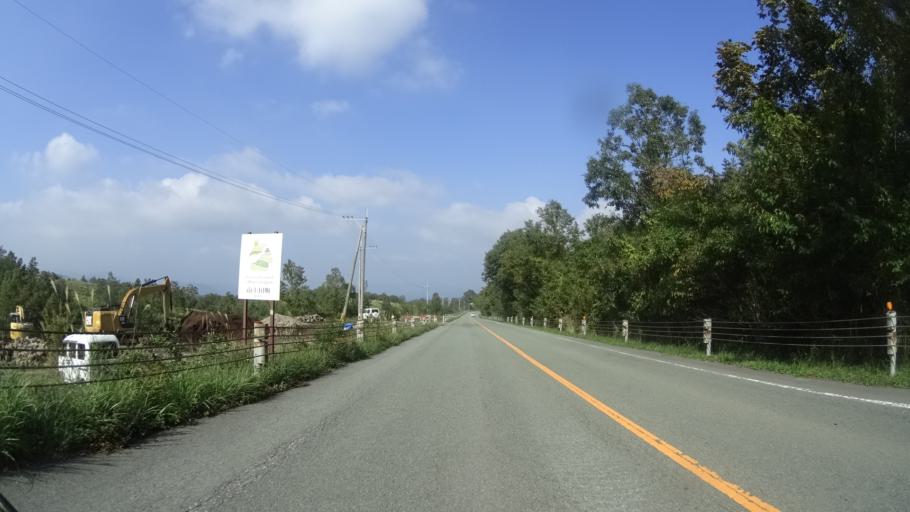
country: JP
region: Kumamoto
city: Aso
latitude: 33.0319
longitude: 131.0643
